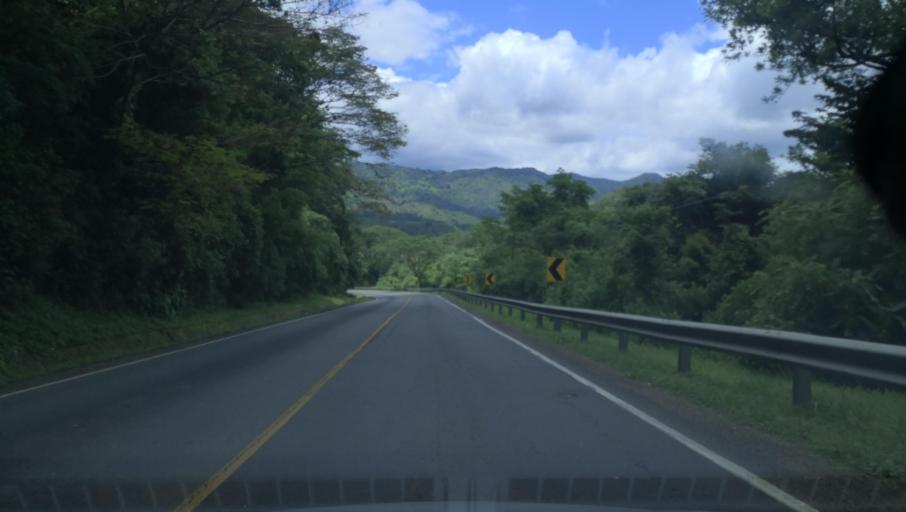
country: NI
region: Esteli
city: Condega
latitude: 13.2499
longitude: -86.3574
